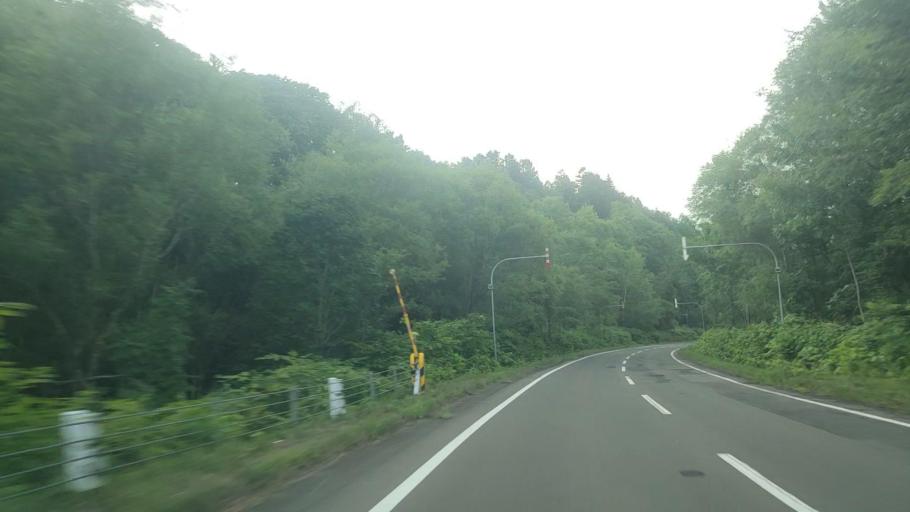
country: JP
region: Hokkaido
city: Bibai
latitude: 43.1155
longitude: 142.0988
